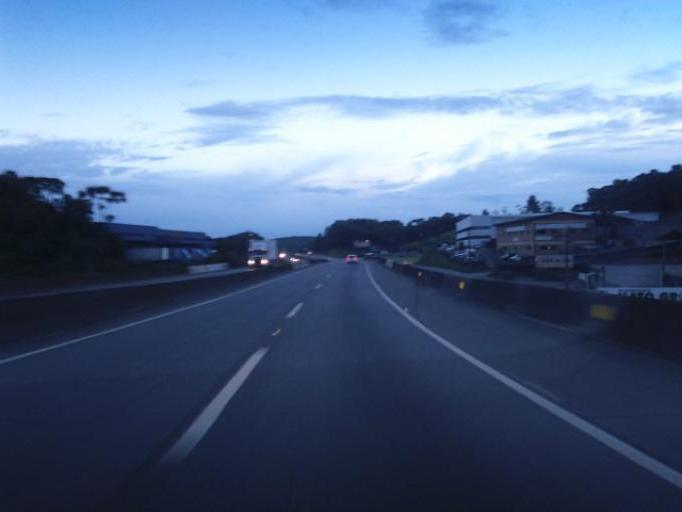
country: BR
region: Santa Catarina
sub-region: Joinville
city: Joinville
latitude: -26.3375
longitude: -48.8594
